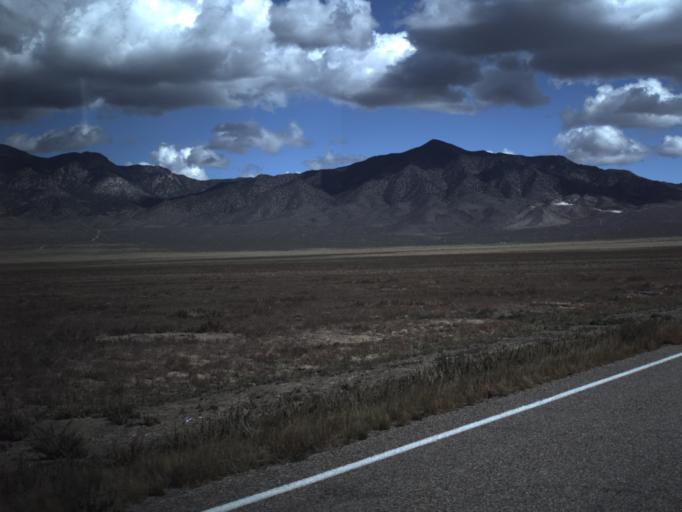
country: US
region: Utah
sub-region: Beaver County
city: Milford
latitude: 38.4605
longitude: -113.3762
